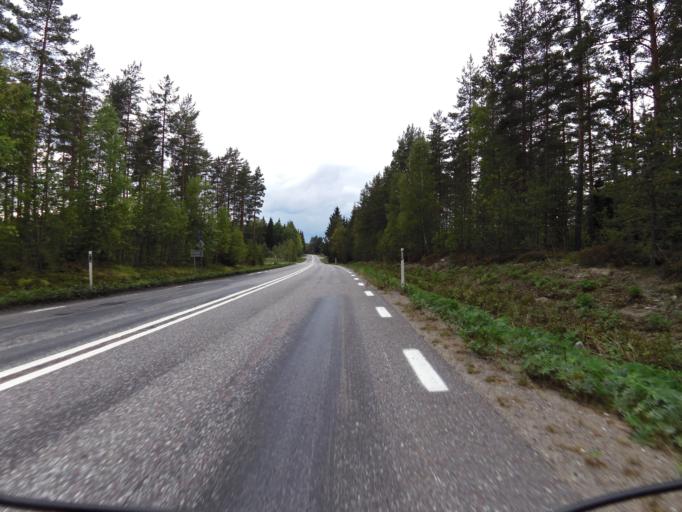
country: SE
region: Gaevleborg
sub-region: Ockelbo Kommun
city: Ockelbo
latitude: 60.8861
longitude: 16.8060
